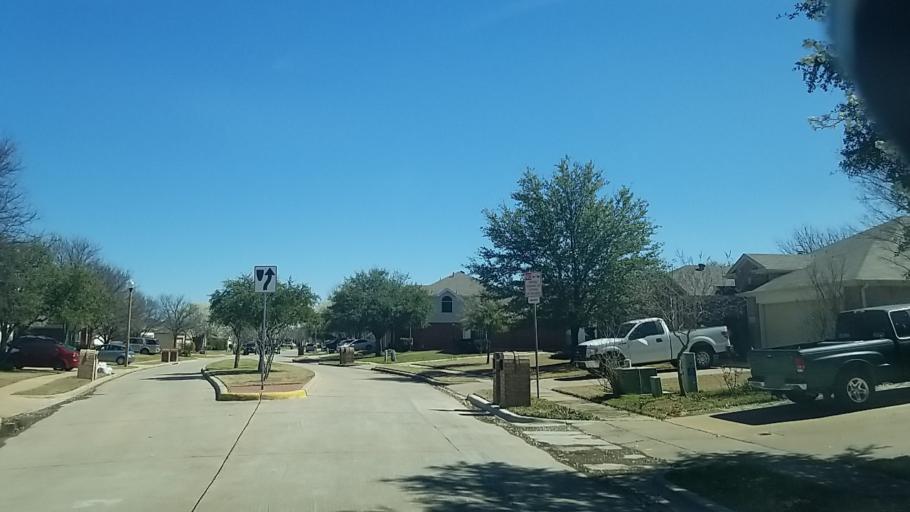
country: US
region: Texas
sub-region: Denton County
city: Corinth
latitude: 33.1745
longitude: -97.1077
